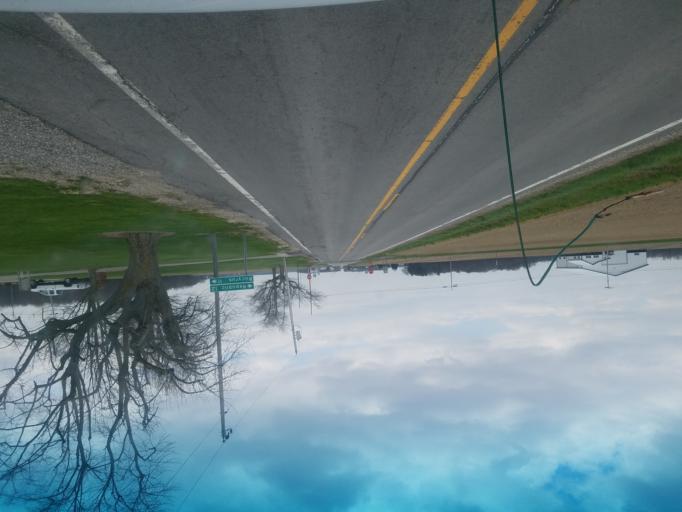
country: US
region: Ohio
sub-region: Crawford County
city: Bucyrus
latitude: 40.9503
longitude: -83.0179
